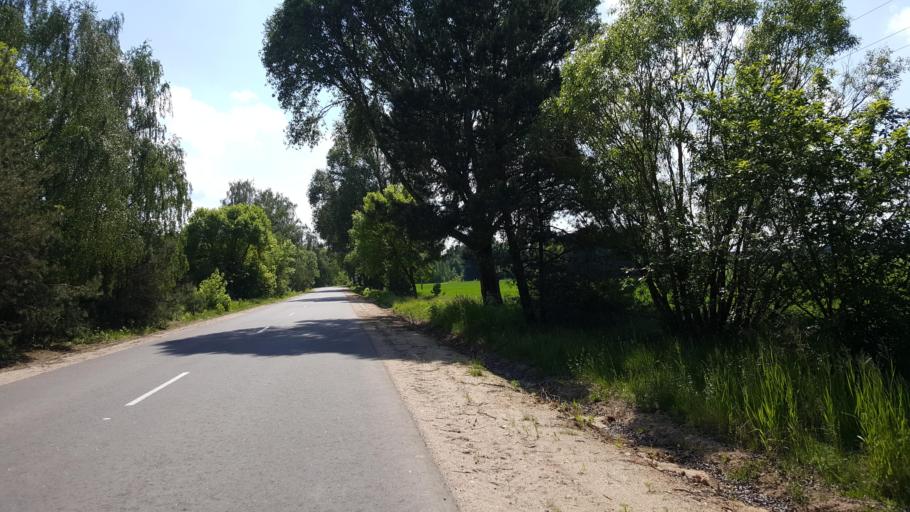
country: BY
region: Brest
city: Kamyanyets
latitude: 52.4024
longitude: 23.9034
